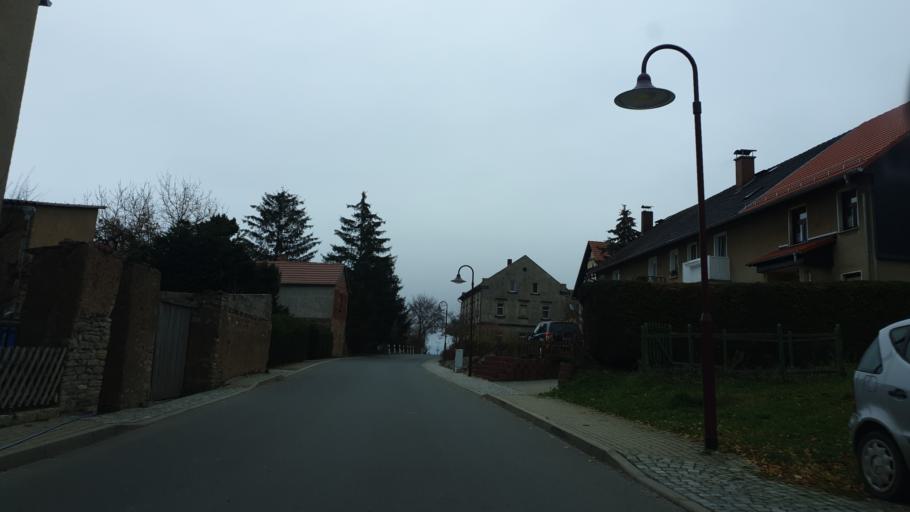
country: DE
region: Thuringia
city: Rauda
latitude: 50.9765
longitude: 11.9443
